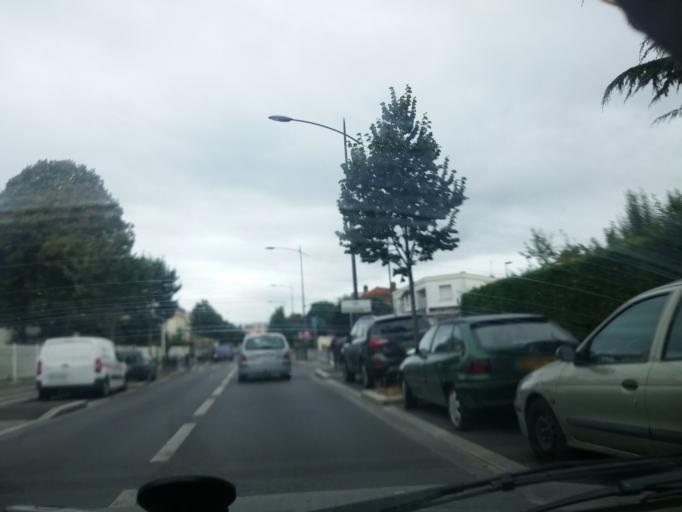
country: FR
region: Ile-de-France
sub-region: Departement du Val-de-Marne
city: Chevilly-Larue
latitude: 48.7682
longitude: 2.3729
